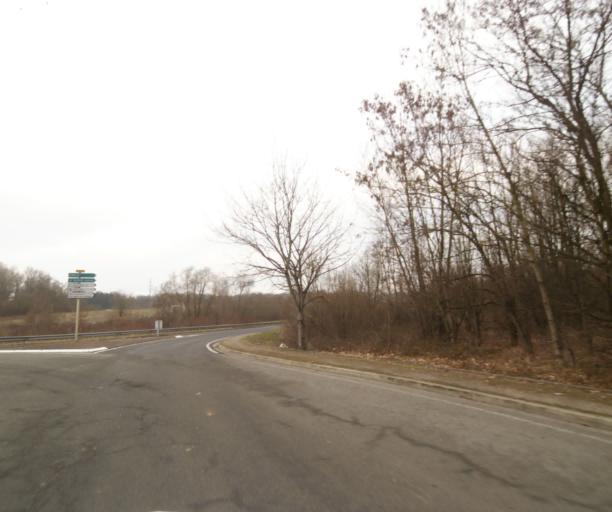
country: FR
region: Lorraine
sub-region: Departement de la Meuse
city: Ancerville
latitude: 48.6379
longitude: 5.0129
